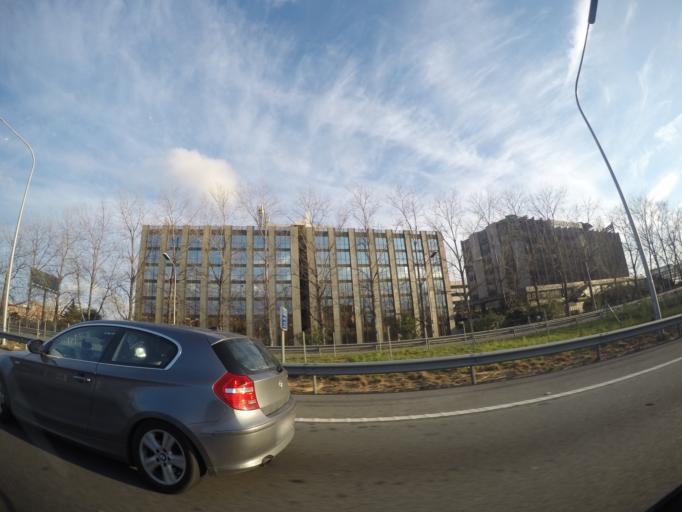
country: ES
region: Catalonia
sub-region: Provincia de Barcelona
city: Sant Joan Despi
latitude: 41.3757
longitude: 2.0697
